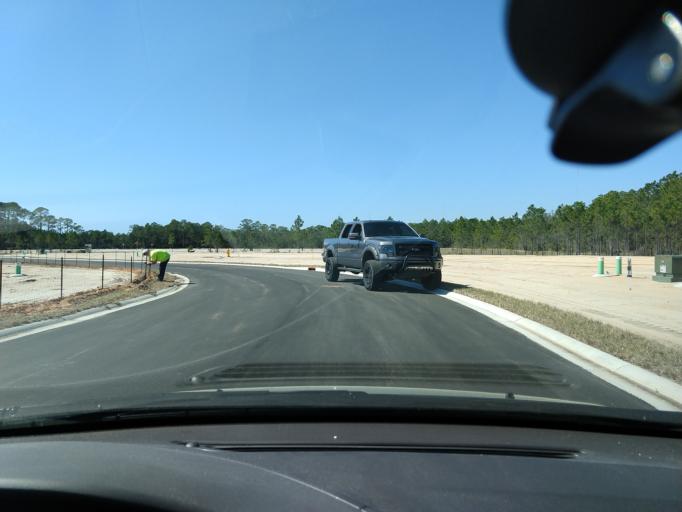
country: US
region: Florida
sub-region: Walton County
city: Miramar Beach
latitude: 30.3832
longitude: -86.2891
